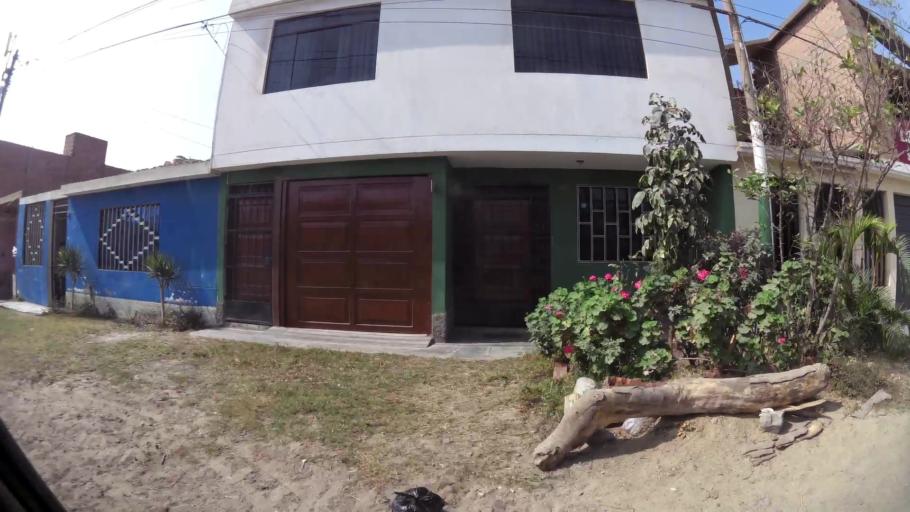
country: PE
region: Lima
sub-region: Lima
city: Santa Rosa
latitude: -11.7821
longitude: -77.1587
